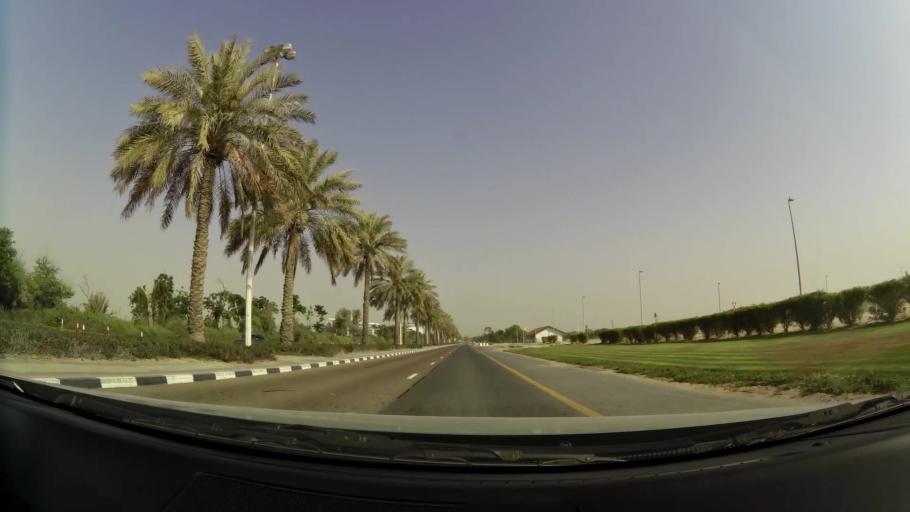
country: AE
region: Dubai
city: Dubai
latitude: 25.1650
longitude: 55.3210
